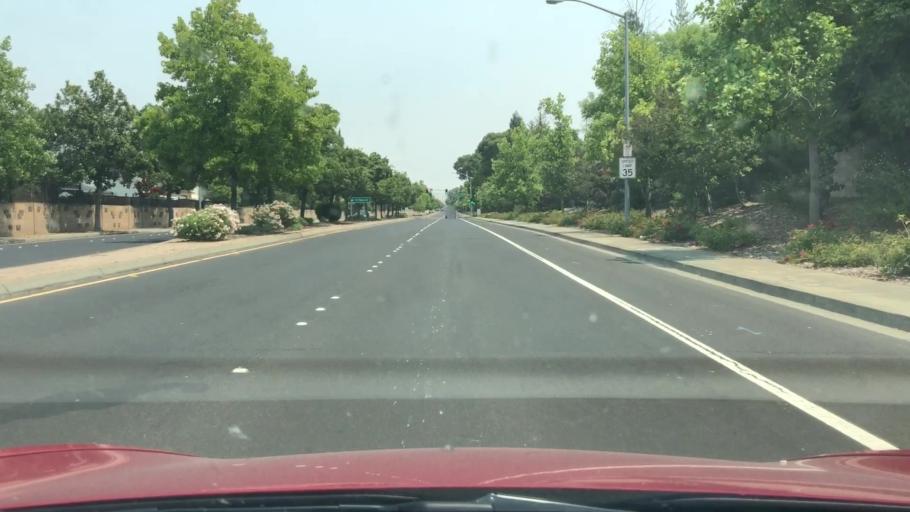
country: US
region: California
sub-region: Alameda County
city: Livermore
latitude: 37.6607
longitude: -121.7946
